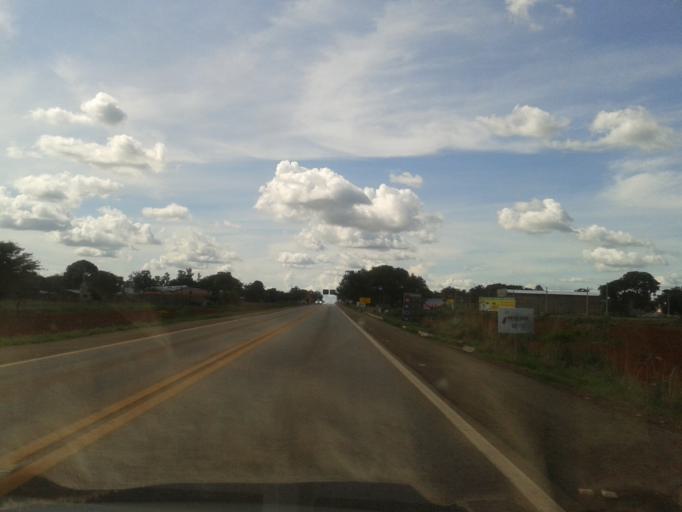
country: BR
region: Goias
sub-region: Mozarlandia
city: Mozarlandia
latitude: -15.1029
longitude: -50.6126
